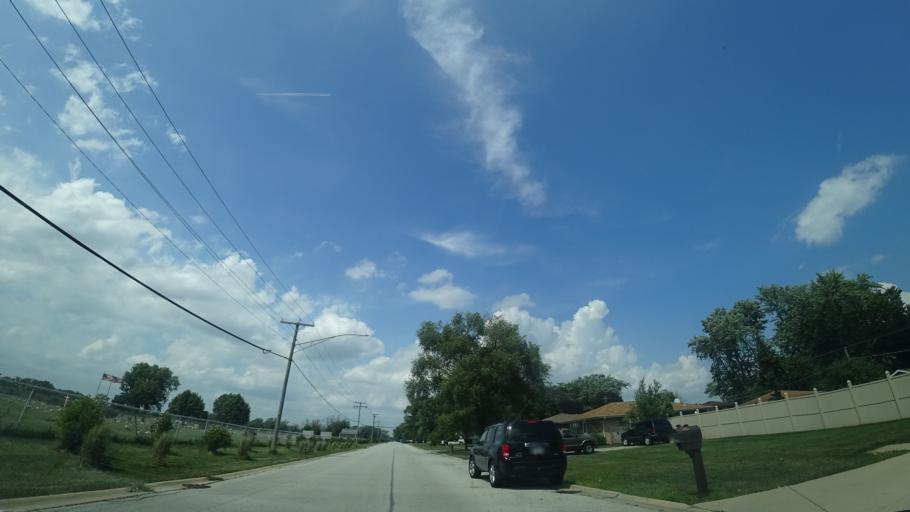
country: US
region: Illinois
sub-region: Cook County
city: Alsip
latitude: 41.6767
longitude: -87.7490
